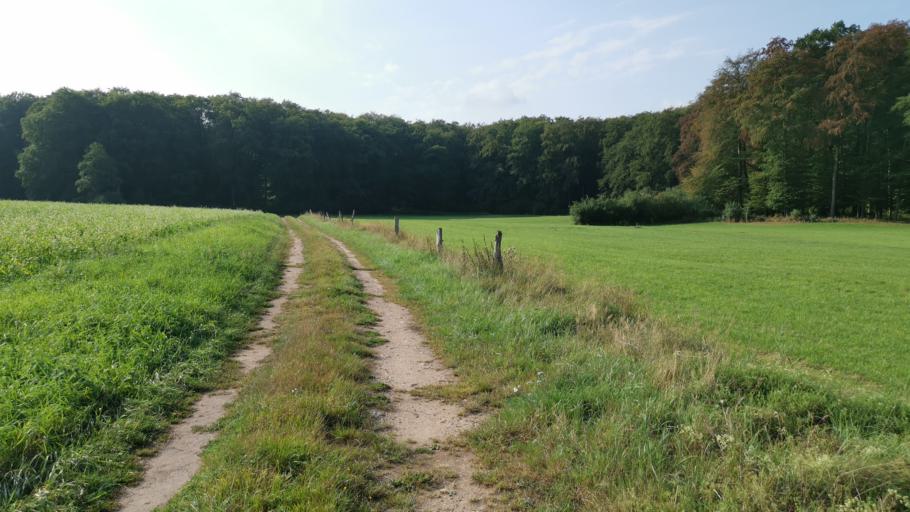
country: DE
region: Schleswig-Holstein
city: Sterley
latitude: 53.6078
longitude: 10.7954
